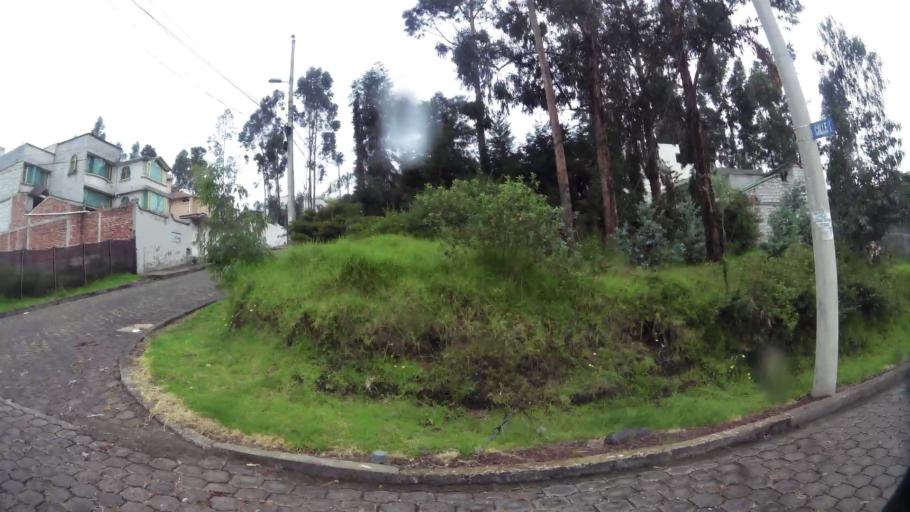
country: EC
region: Pichincha
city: Sangolqui
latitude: -0.3241
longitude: -78.4322
